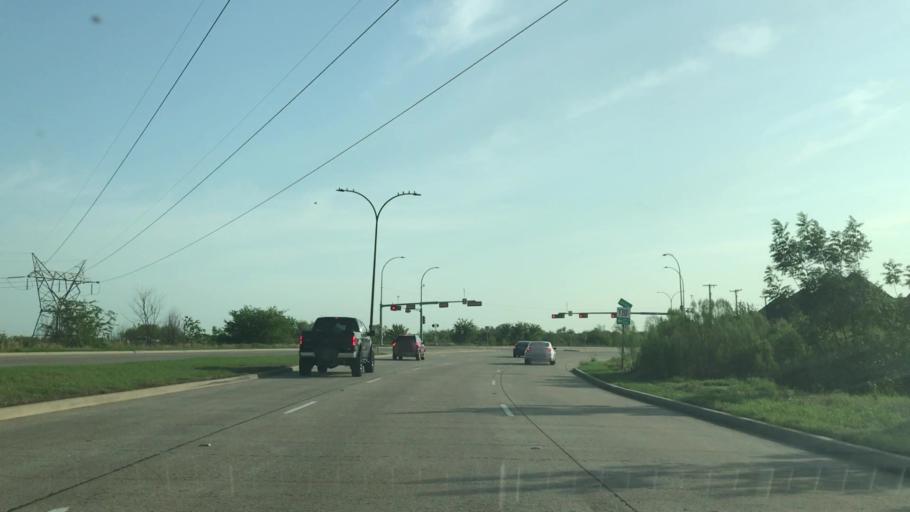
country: US
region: Texas
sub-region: Tarrant County
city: Arlington
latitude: 32.7778
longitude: -97.1360
